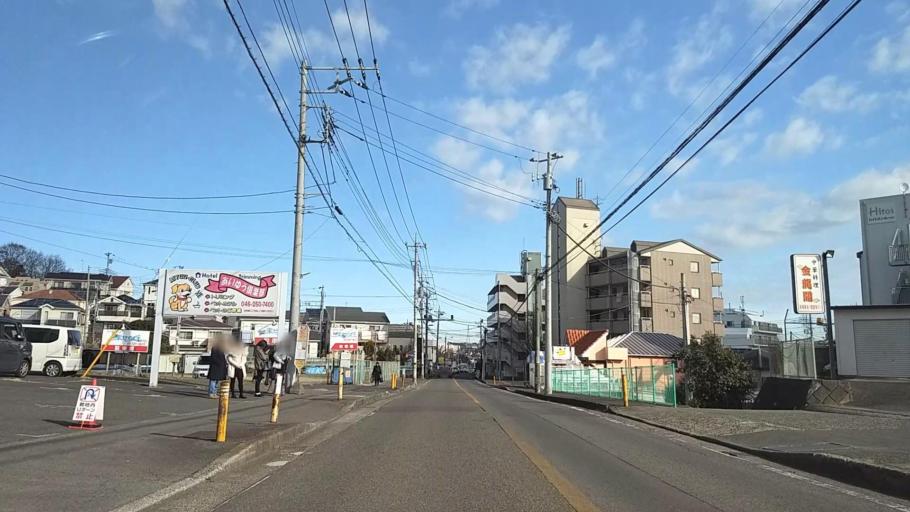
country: JP
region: Kanagawa
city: Atsugi
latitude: 35.4346
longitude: 139.3373
